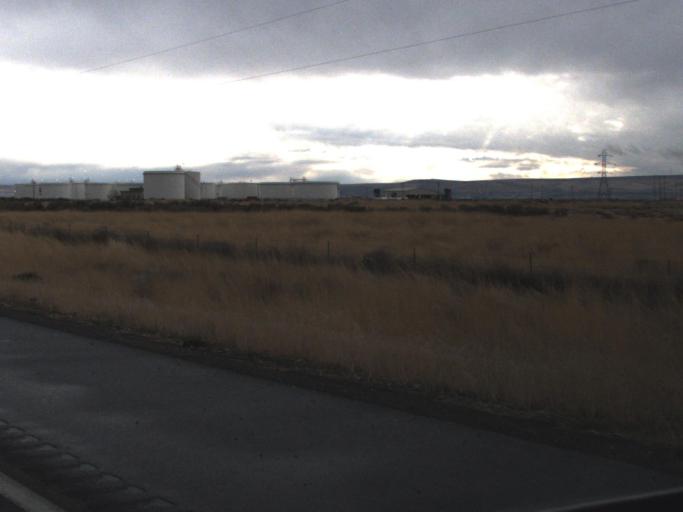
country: US
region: Washington
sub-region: Walla Walla County
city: Burbank
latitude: 46.2217
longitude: -119.0314
